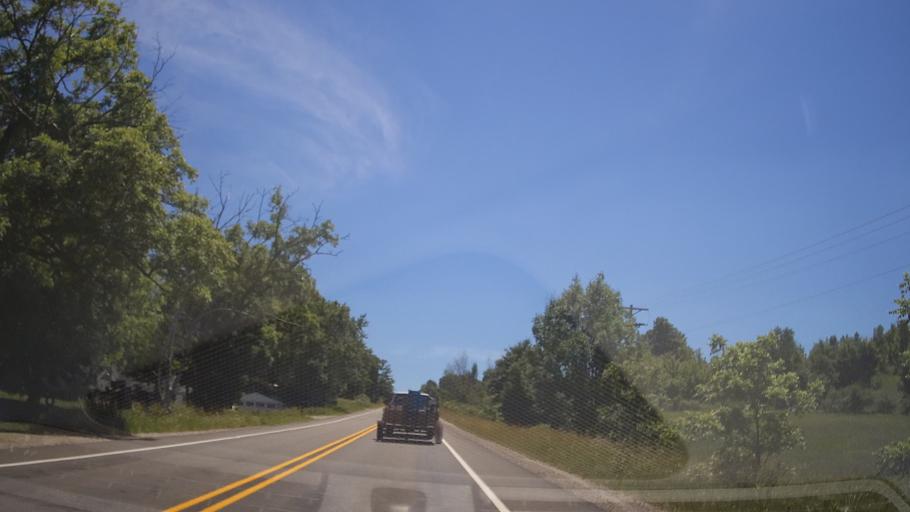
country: US
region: Michigan
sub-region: Grand Traverse County
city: Traverse City
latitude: 44.6220
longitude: -85.6965
